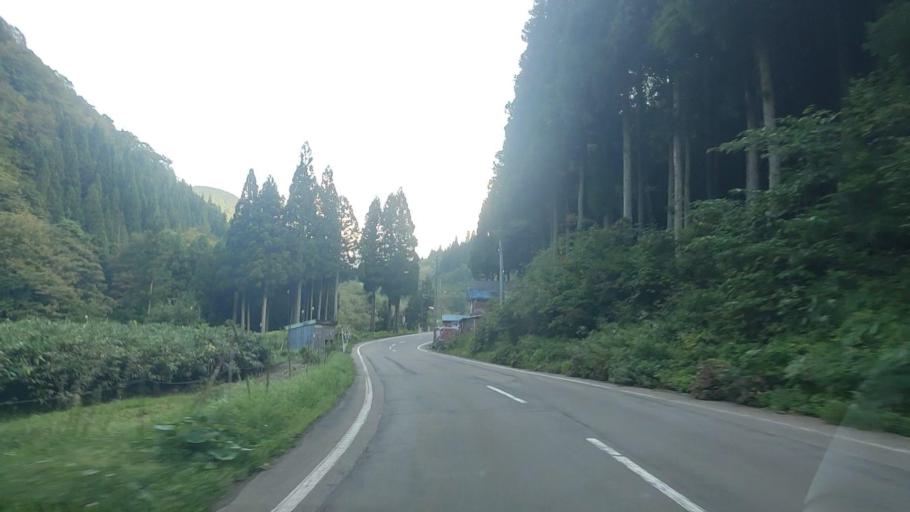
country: JP
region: Toyama
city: Yatsuomachi-higashikumisaka
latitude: 36.4951
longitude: 137.0492
